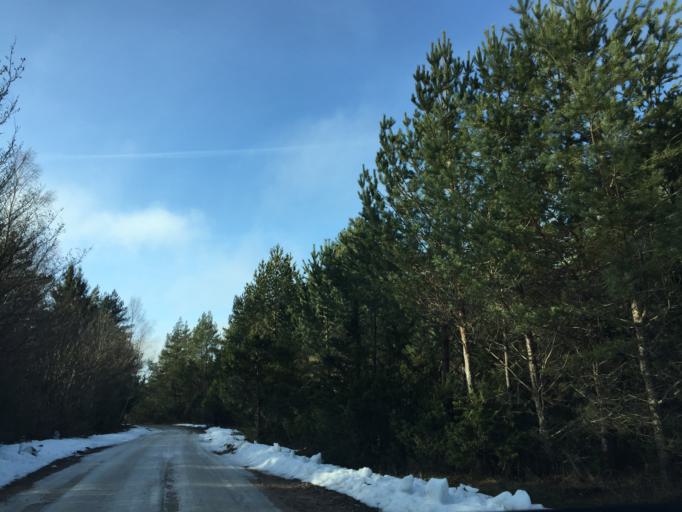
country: EE
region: Saare
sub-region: Kuressaare linn
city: Kuressaare
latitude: 58.4705
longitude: 21.9736
